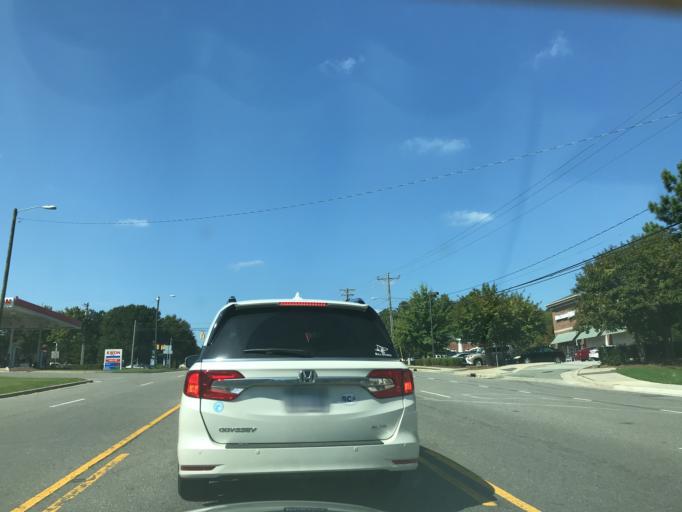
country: US
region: North Carolina
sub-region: Durham County
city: Durham
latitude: 35.9104
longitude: -78.9331
